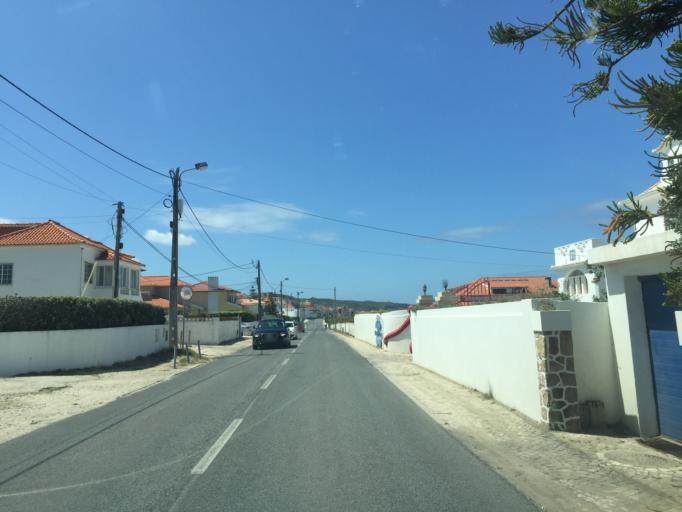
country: PT
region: Lisbon
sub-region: Sintra
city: Colares
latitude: 38.8323
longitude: -9.4673
